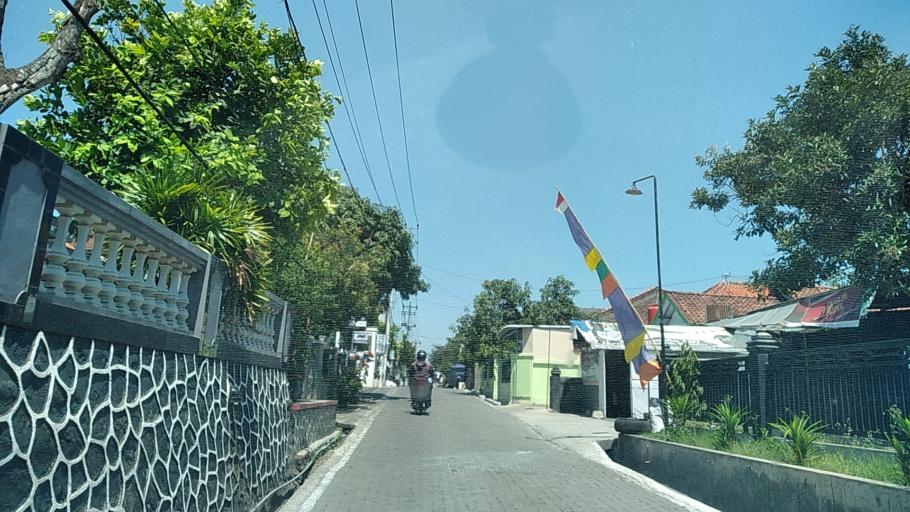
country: ID
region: Central Java
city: Ungaran
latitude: -7.0958
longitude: 110.4117
